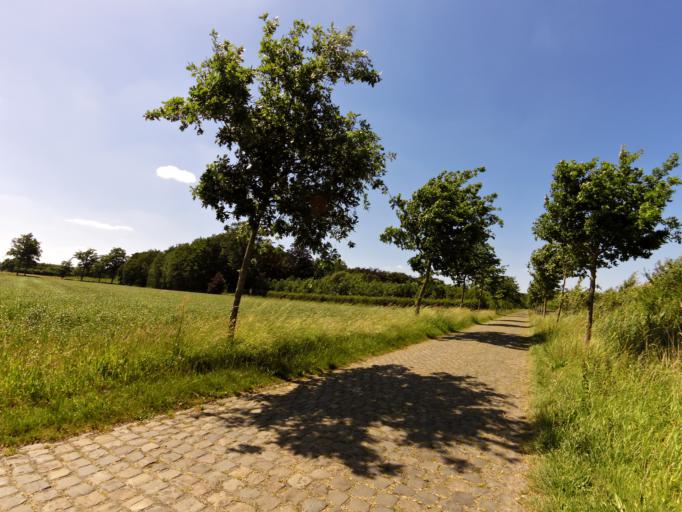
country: BE
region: Flanders
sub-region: Provincie West-Vlaanderen
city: Zedelgem
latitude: 51.1430
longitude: 3.1178
